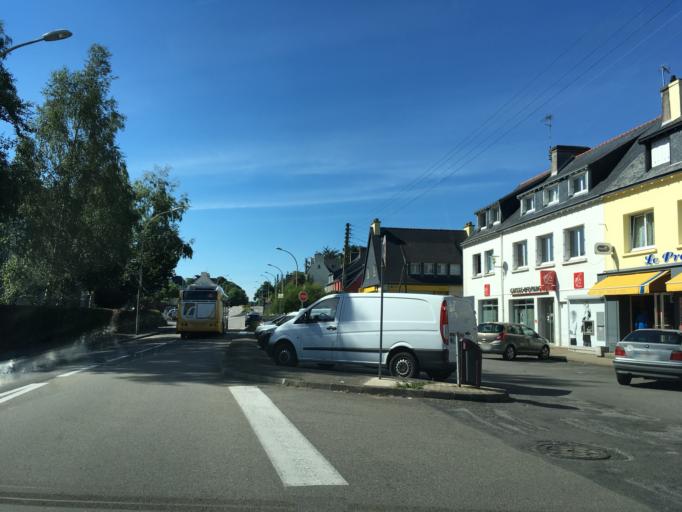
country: FR
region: Brittany
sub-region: Departement du Finistere
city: Quimper
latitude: 47.9837
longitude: -4.1044
